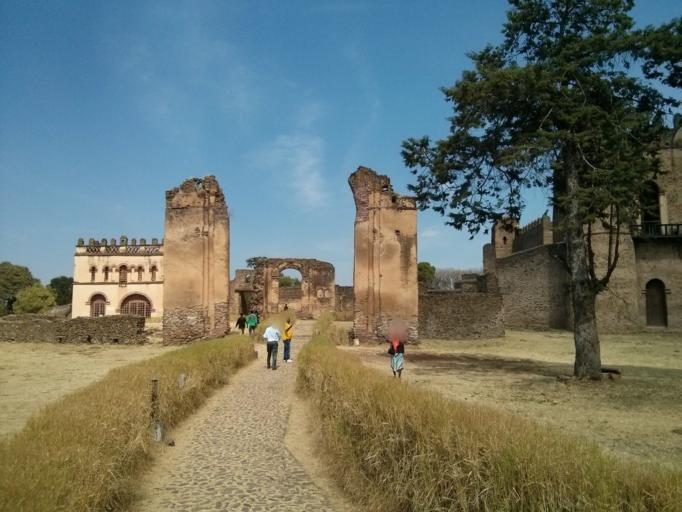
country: ET
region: Amhara
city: Gondar
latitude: 12.6073
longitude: 37.4694
